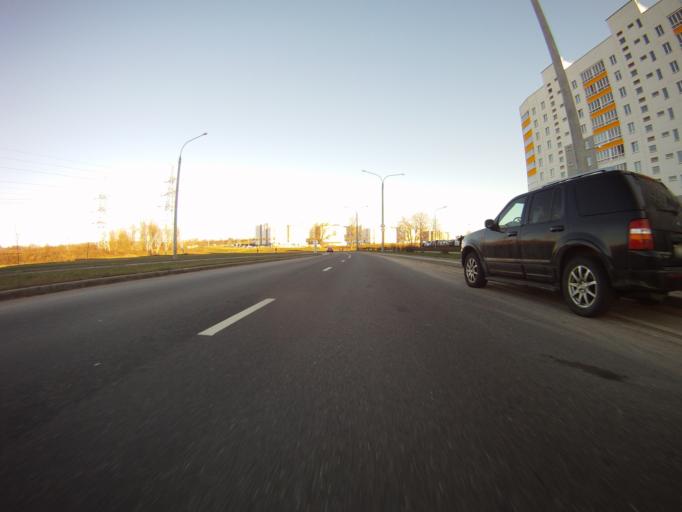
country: BY
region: Minsk
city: Novoye Medvezhino
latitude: 53.8753
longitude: 27.4690
